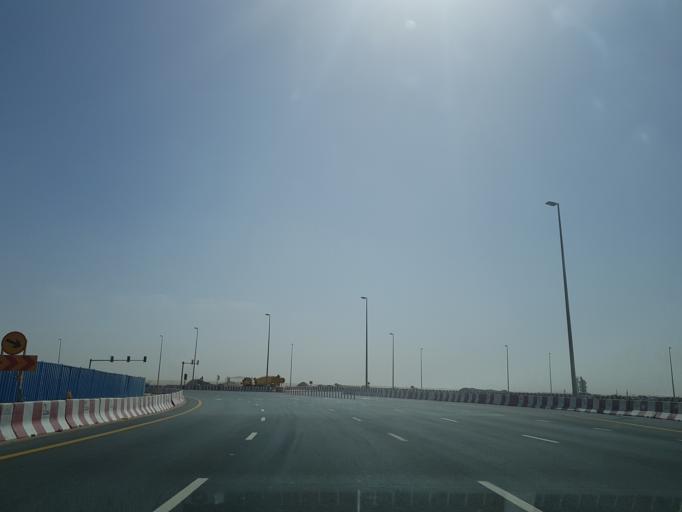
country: AE
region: Dubai
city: Dubai
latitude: 24.9614
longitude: 55.1790
